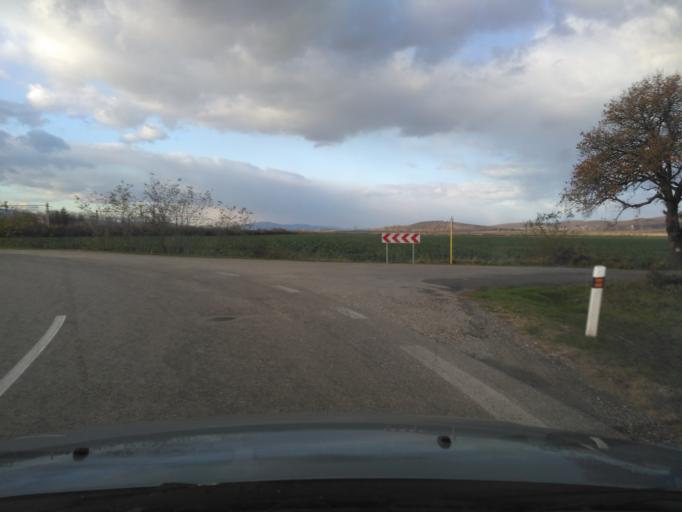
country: HU
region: Borsod-Abauj-Zemplen
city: Satoraljaujhely
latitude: 48.4116
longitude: 21.6677
